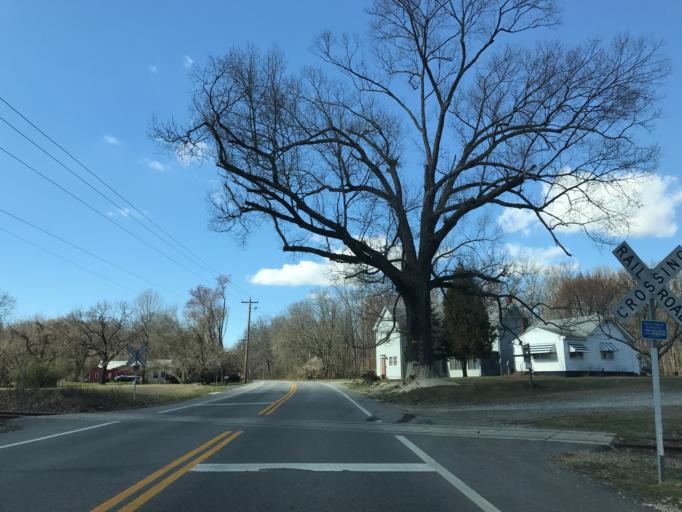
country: US
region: Maryland
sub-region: Queen Anne's County
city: Kingstown
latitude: 39.1171
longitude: -75.9177
